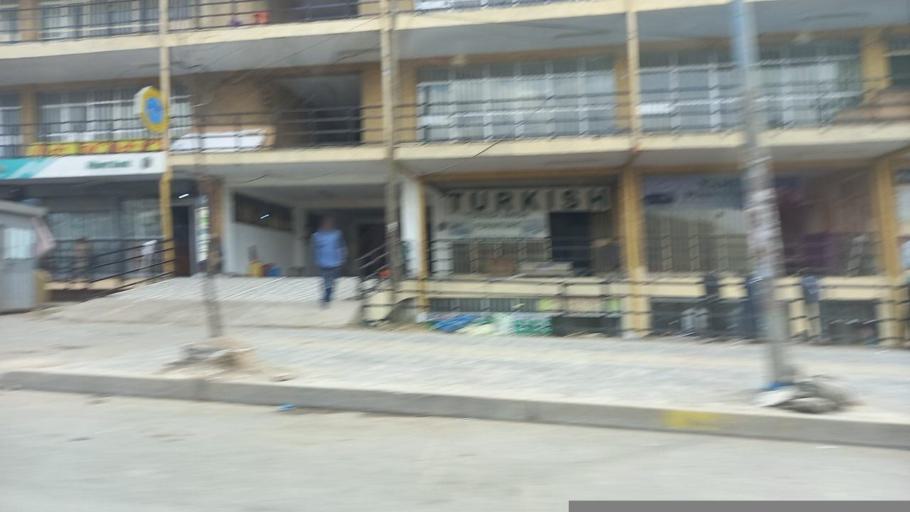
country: ET
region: Adis Abeba
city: Addis Ababa
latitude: 9.0208
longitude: 38.8693
